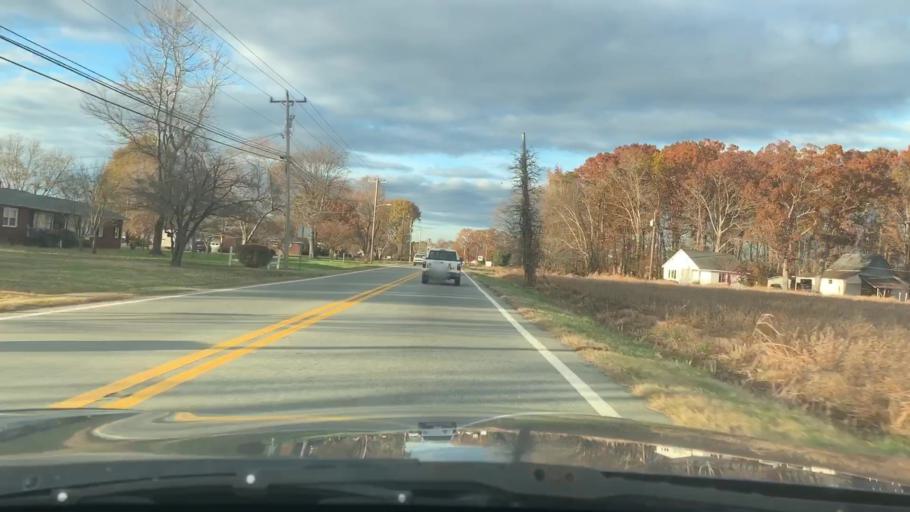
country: US
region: North Carolina
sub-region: Alamance County
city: Green Level
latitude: 36.1090
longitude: -79.3532
